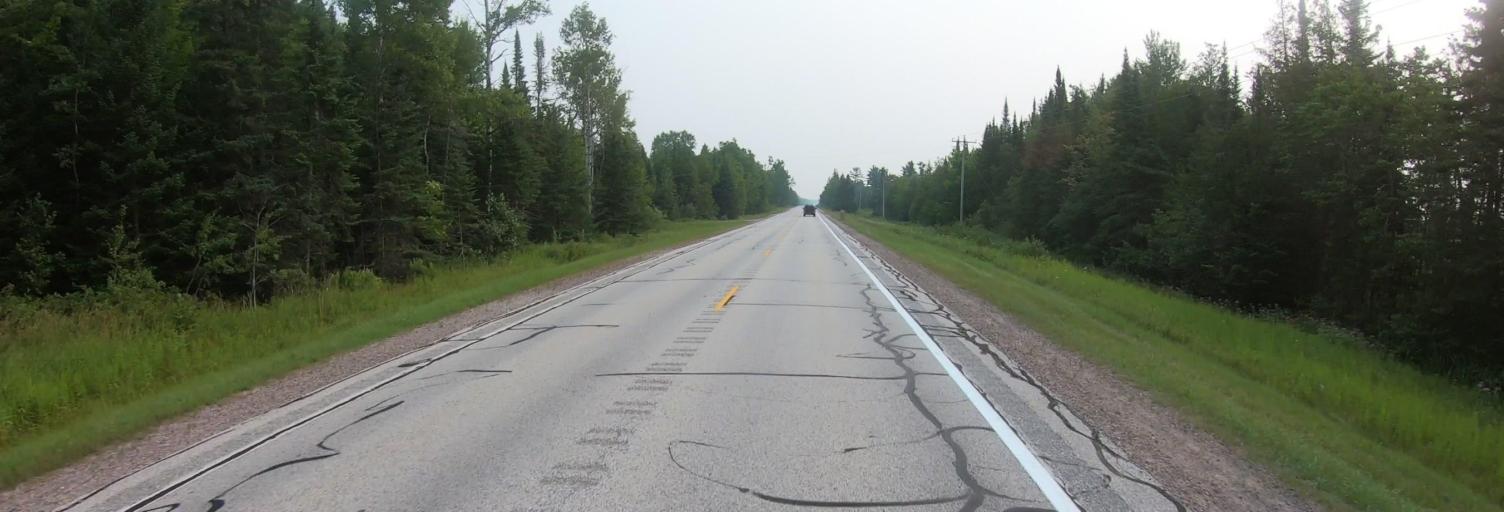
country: US
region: Michigan
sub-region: Luce County
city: Newberry
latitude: 46.5131
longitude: -85.0872
